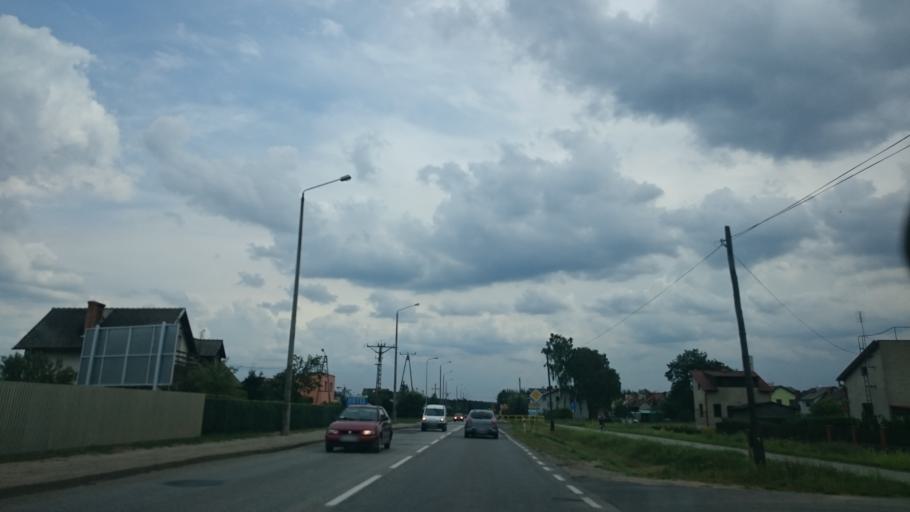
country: PL
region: Kujawsko-Pomorskie
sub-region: Powiat tucholski
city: Tuchola
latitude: 53.5709
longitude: 17.8886
